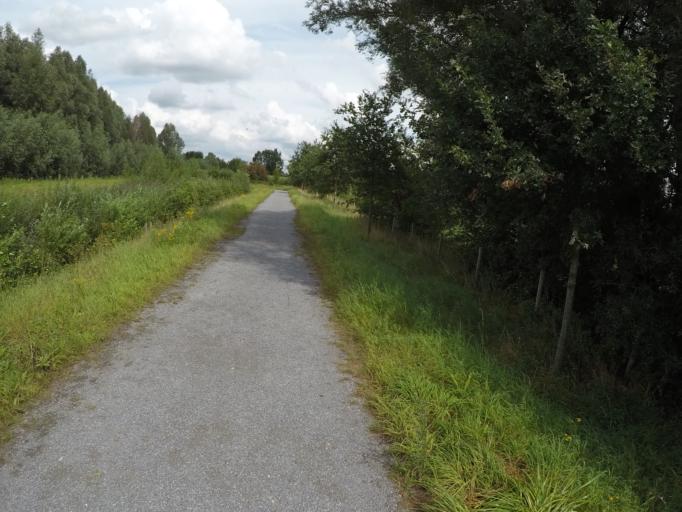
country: BE
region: Flanders
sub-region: Provincie Antwerpen
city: Lier
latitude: 51.1495
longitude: 4.5495
